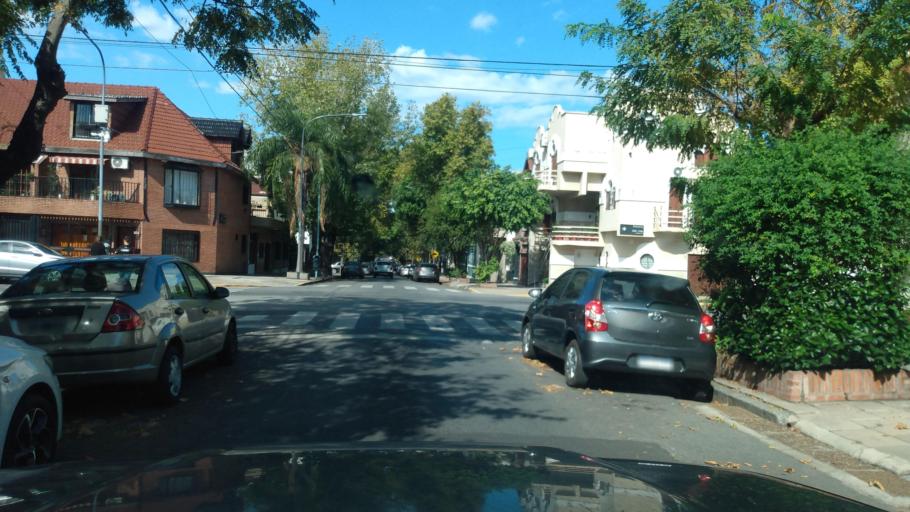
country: AR
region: Buenos Aires F.D.
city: Villa Santa Rita
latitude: -34.5820
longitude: -58.4869
